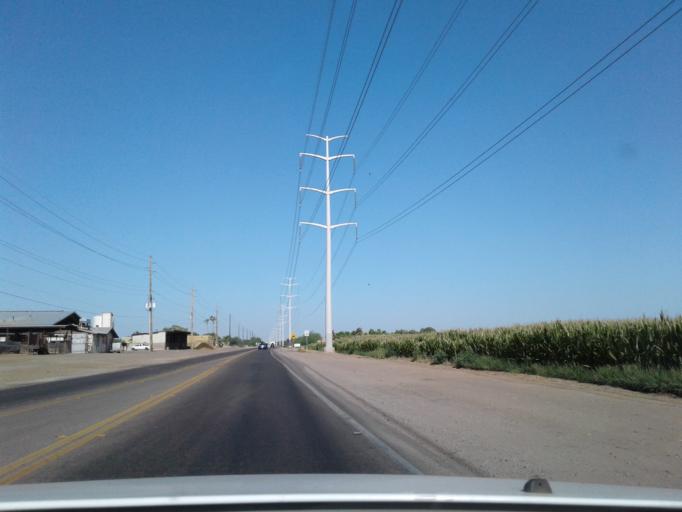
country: US
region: Arizona
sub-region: Maricopa County
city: Laveen
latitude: 33.4085
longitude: -112.2051
